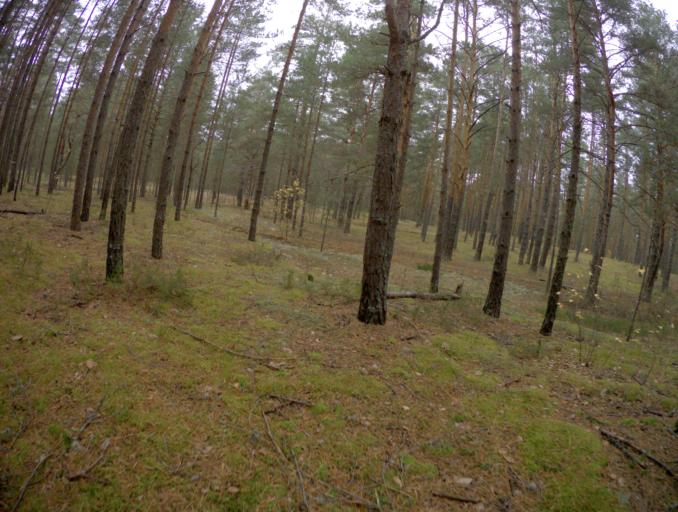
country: RU
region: Vladimir
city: Kommunar
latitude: 56.0815
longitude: 40.4386
